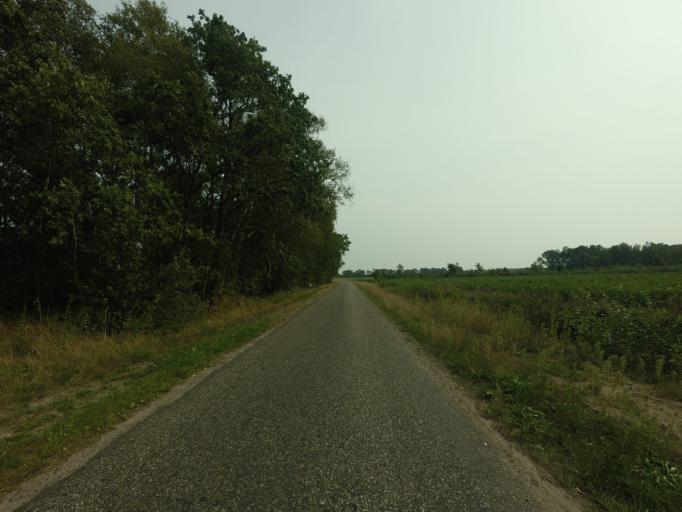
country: NL
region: Drenthe
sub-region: Gemeente Tynaarlo
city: Vries
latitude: 53.1083
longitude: 6.5455
